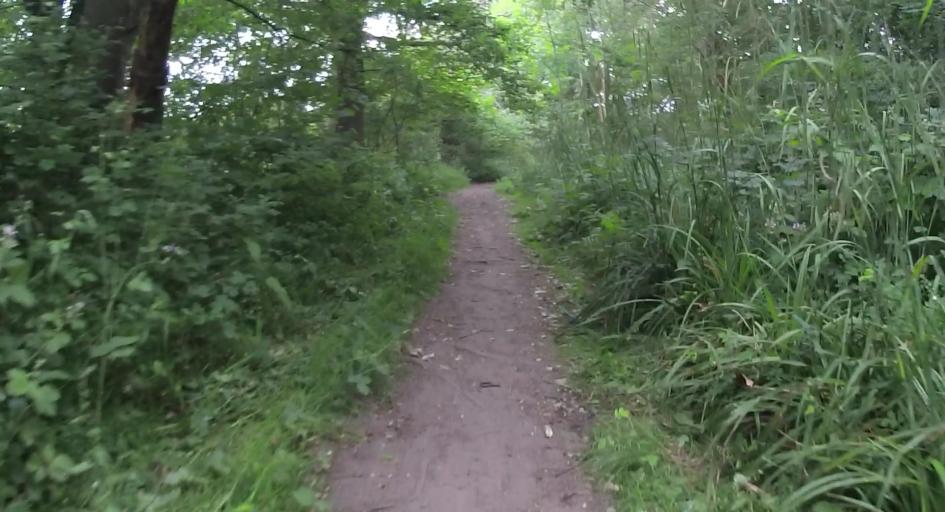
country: GB
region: England
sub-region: Surrey
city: Seale
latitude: 51.2392
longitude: -0.7228
